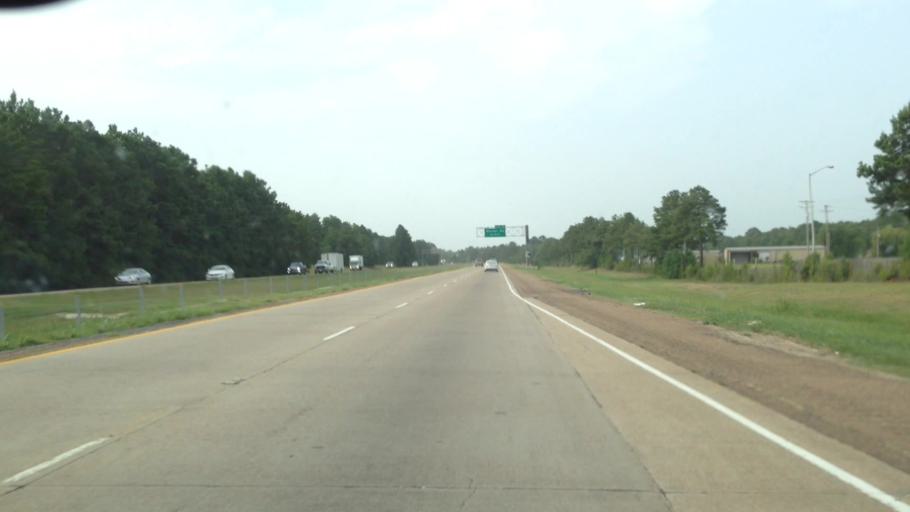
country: US
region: Louisiana
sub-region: Caddo Parish
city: Shreveport
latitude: 32.4366
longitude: -93.8411
